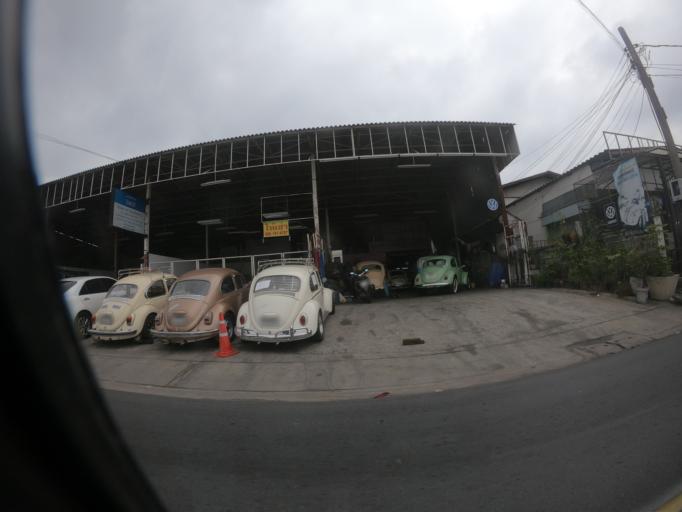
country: TH
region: Bangkok
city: Lat Phrao
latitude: 13.8212
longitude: 100.6006
